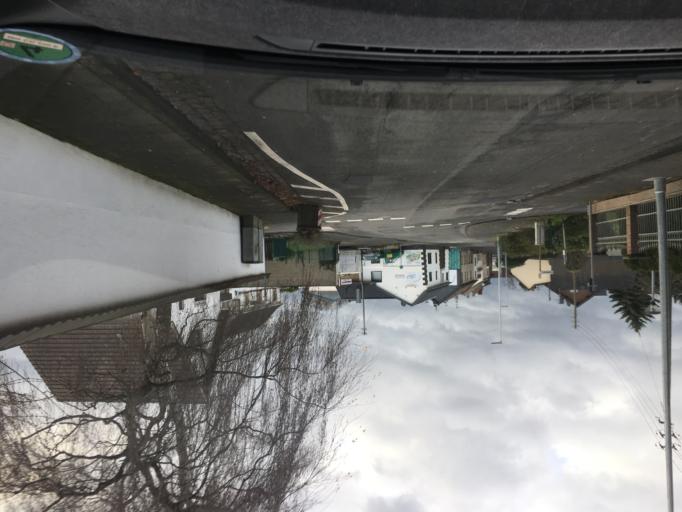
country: DE
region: North Rhine-Westphalia
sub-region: Regierungsbezirk Koln
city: Euskirchen
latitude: 50.6089
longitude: 6.8329
